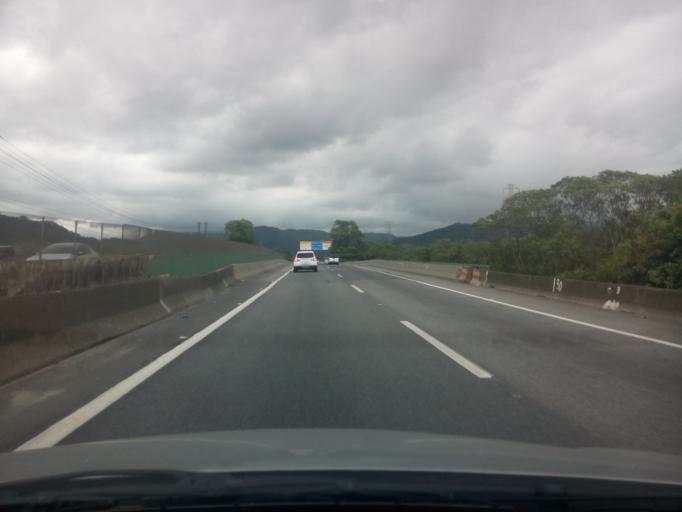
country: BR
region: Sao Paulo
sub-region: Santos
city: Santos
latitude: -23.9035
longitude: -46.2969
